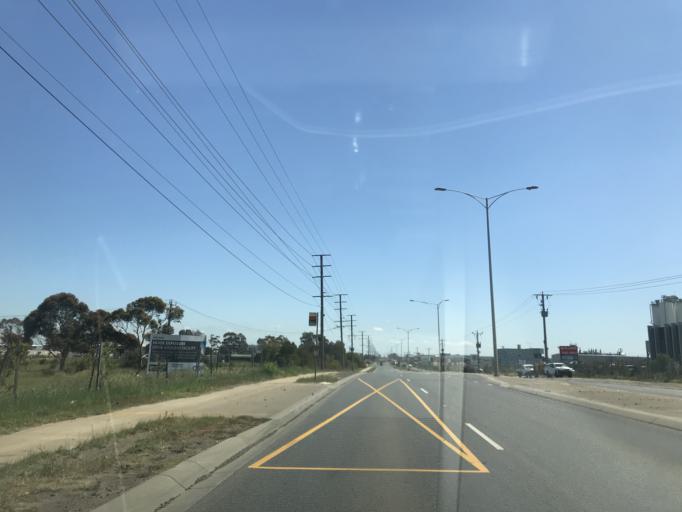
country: AU
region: Victoria
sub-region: Wyndham
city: Truganina
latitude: -37.8272
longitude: 144.7749
